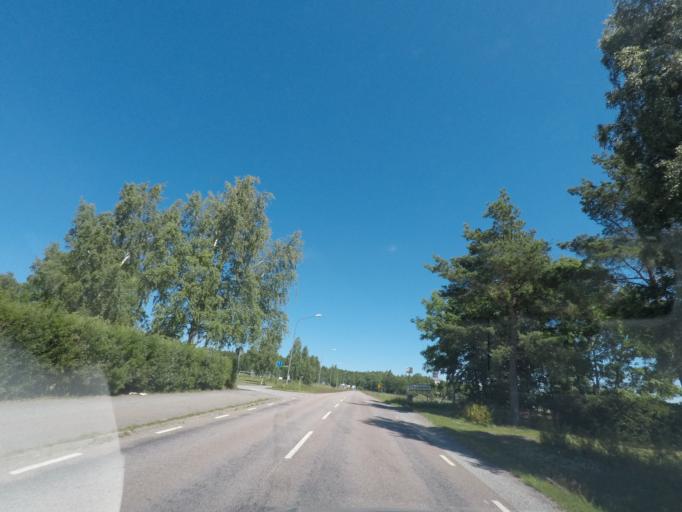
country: SE
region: Vaestmanland
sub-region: Vasteras
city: Tillberga
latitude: 59.6742
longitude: 16.7256
